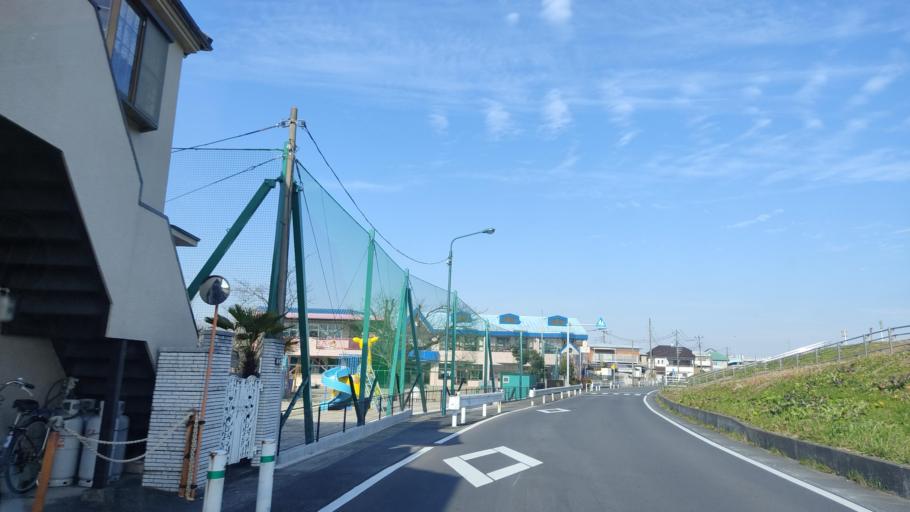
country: JP
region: Chiba
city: Matsudo
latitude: 35.7957
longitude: 139.8865
